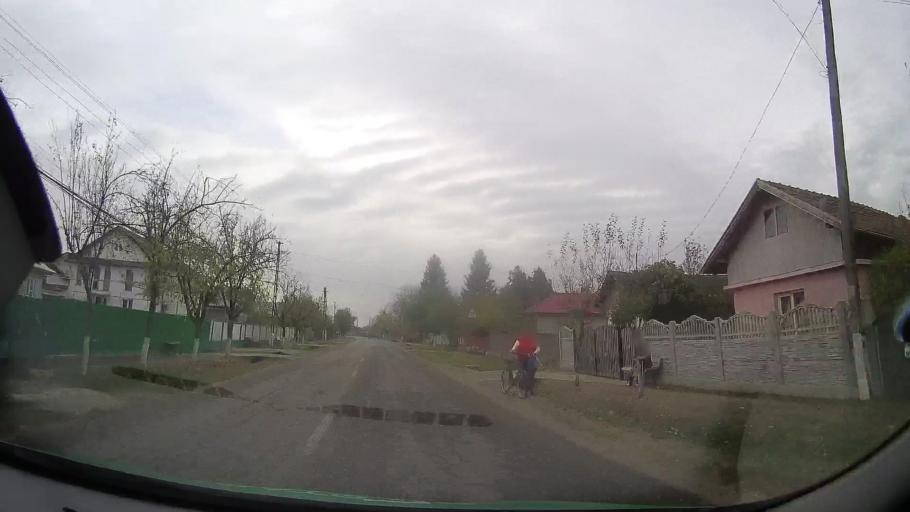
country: RO
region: Prahova
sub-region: Comuna Valea Calugareasca
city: Pantazi
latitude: 44.9186
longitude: 26.1560
